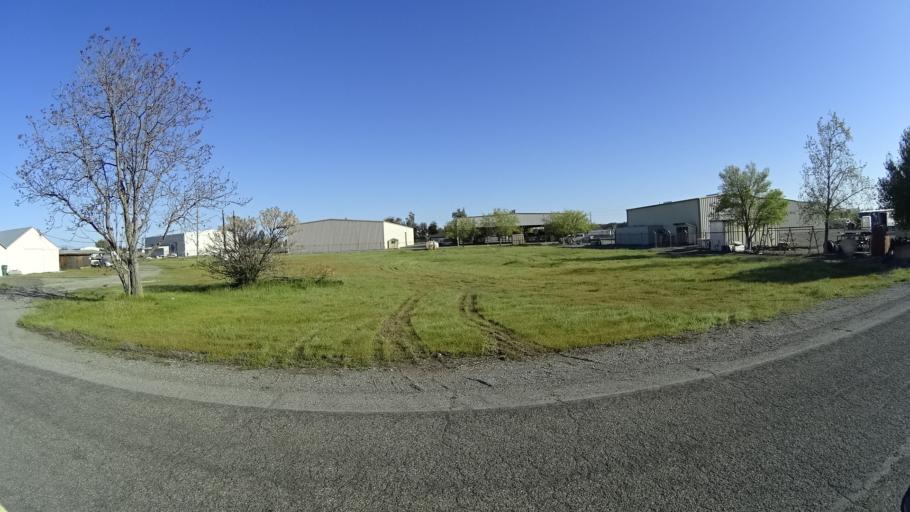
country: US
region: California
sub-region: Glenn County
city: Orland
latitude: 39.7548
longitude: -122.2212
